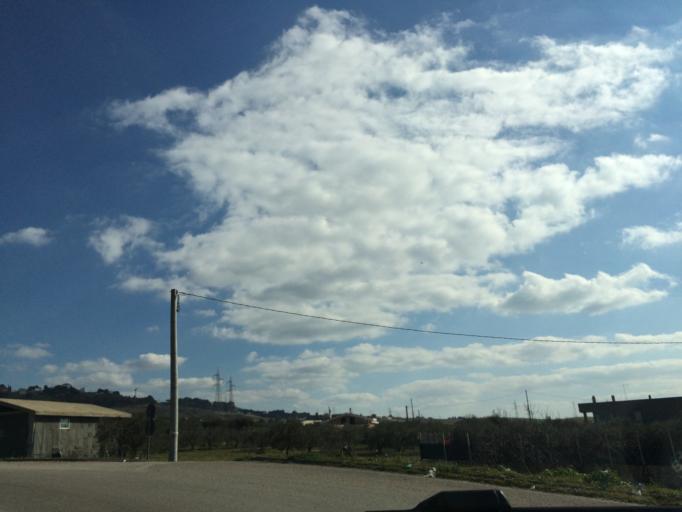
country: IT
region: Basilicate
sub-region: Provincia di Matera
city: Matera
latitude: 40.6687
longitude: 16.5737
